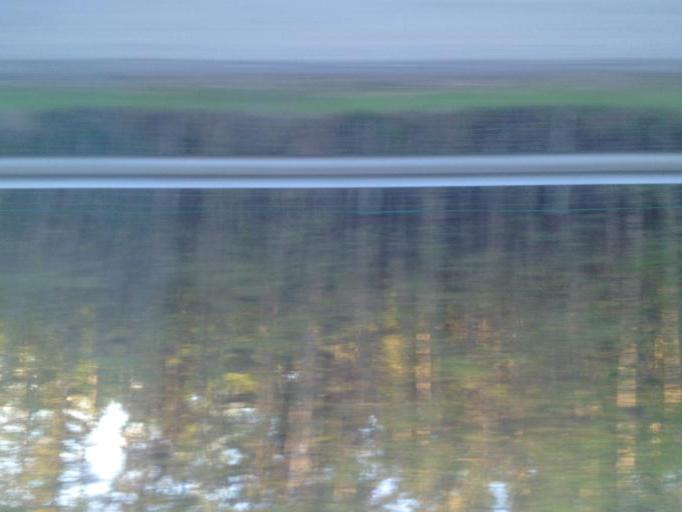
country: FI
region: Haeme
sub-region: Haemeenlinna
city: Parola
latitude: 61.0525
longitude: 24.3529
